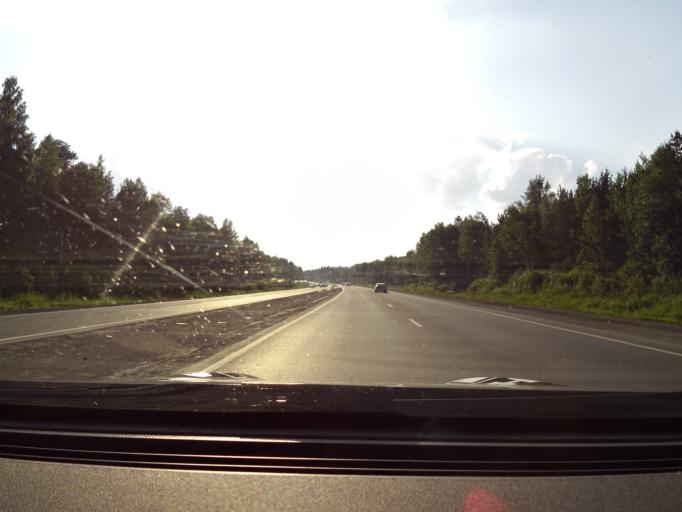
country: RU
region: Sverdlovsk
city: Talitsa
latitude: 56.8464
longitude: 60.0824
